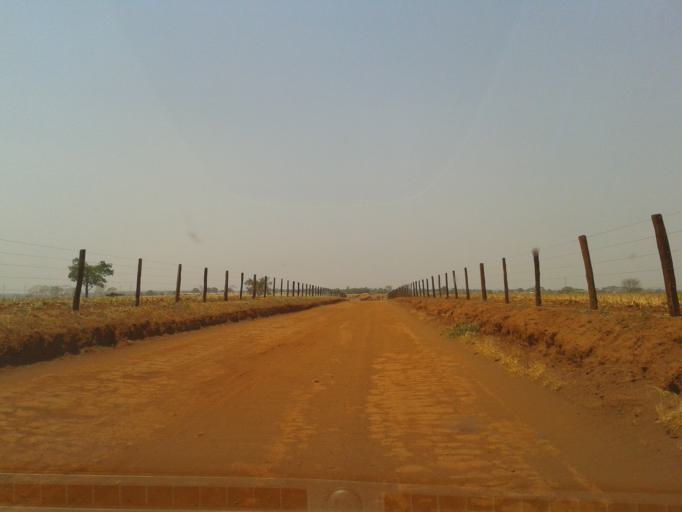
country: BR
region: Minas Gerais
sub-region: Centralina
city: Centralina
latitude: -18.7144
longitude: -49.2215
